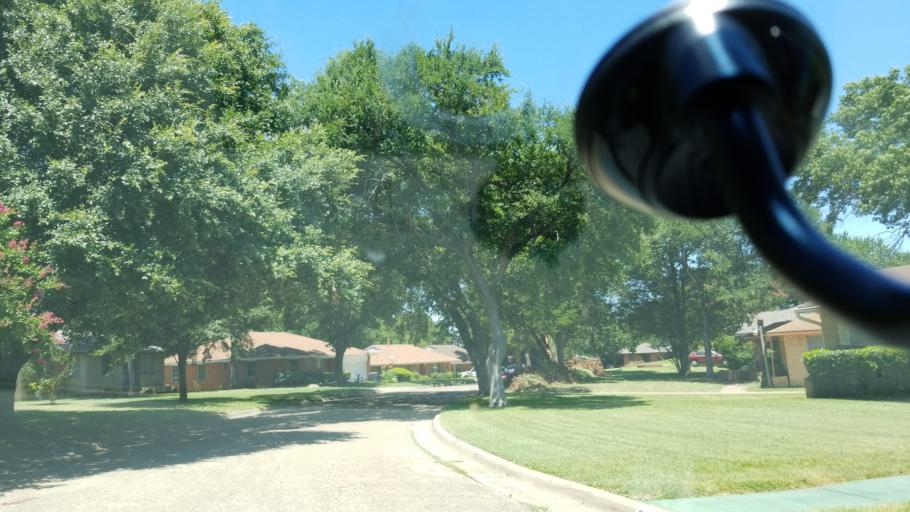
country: US
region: Texas
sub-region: Dallas County
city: Cockrell Hill
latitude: 32.6816
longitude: -96.8180
